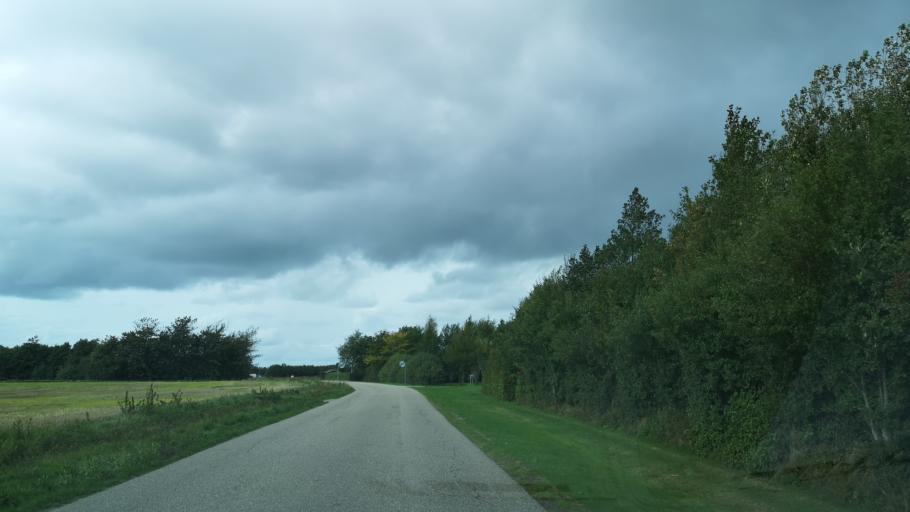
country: DK
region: South Denmark
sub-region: Varde Kommune
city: Oksbol
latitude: 55.8359
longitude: 8.3094
